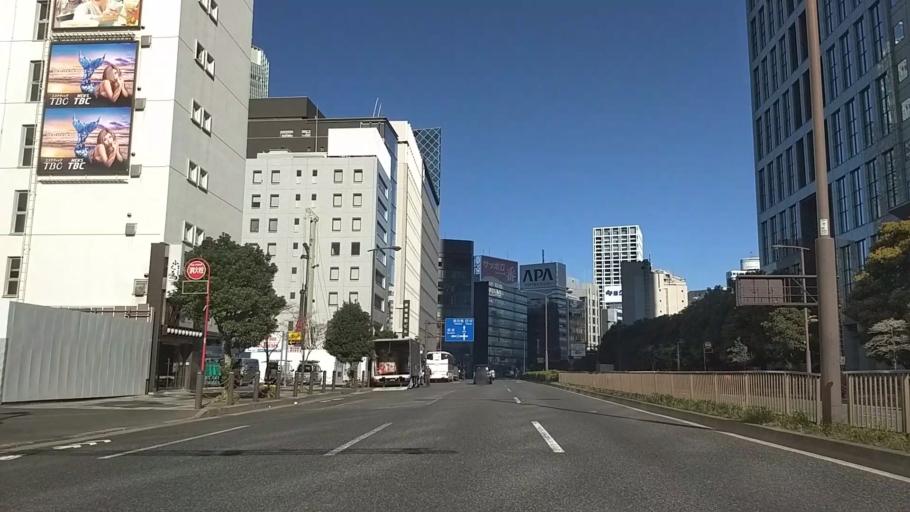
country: JP
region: Tokyo
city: Tokyo
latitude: 35.6722
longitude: 139.7410
